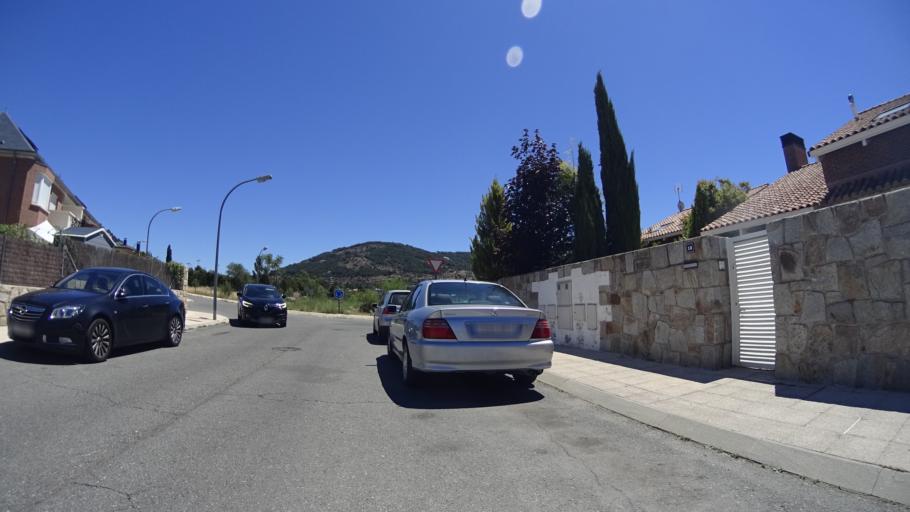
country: ES
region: Madrid
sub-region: Provincia de Madrid
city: Collado Mediano
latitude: 40.6888
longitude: -4.0273
